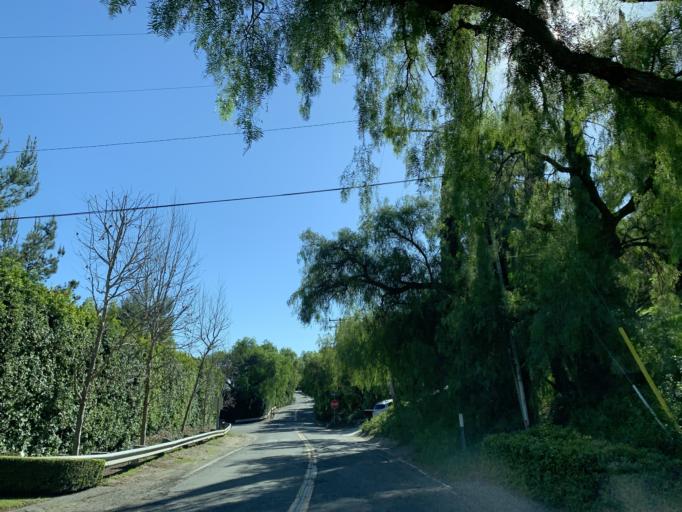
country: US
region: California
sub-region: Orange County
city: Brea
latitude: 33.8925
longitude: -117.9044
